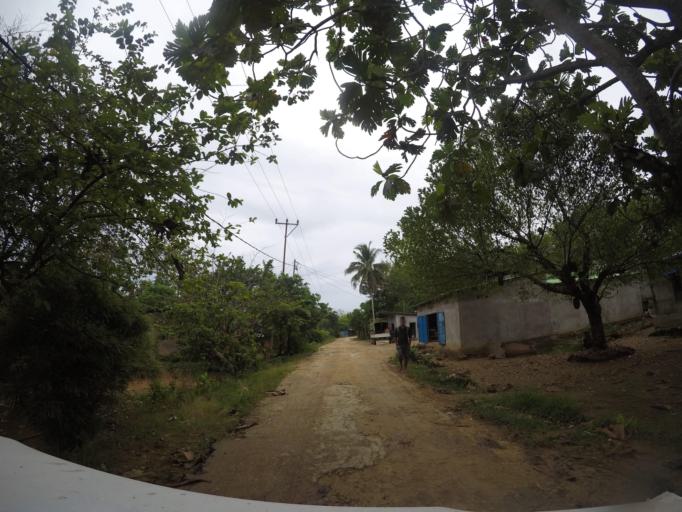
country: TL
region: Lautem
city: Lospalos
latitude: -8.5364
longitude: 126.9967
